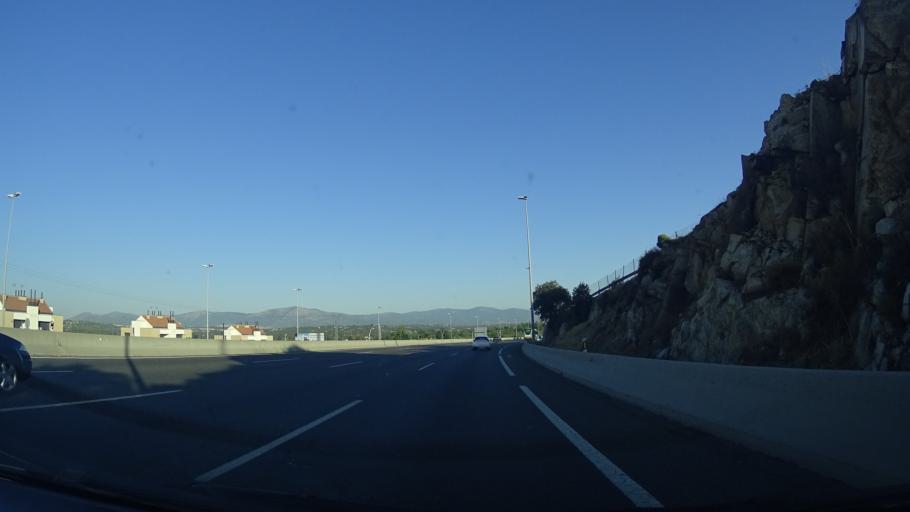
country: ES
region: Madrid
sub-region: Provincia de Madrid
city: Torrelodones
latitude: 40.5792
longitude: -3.9447
